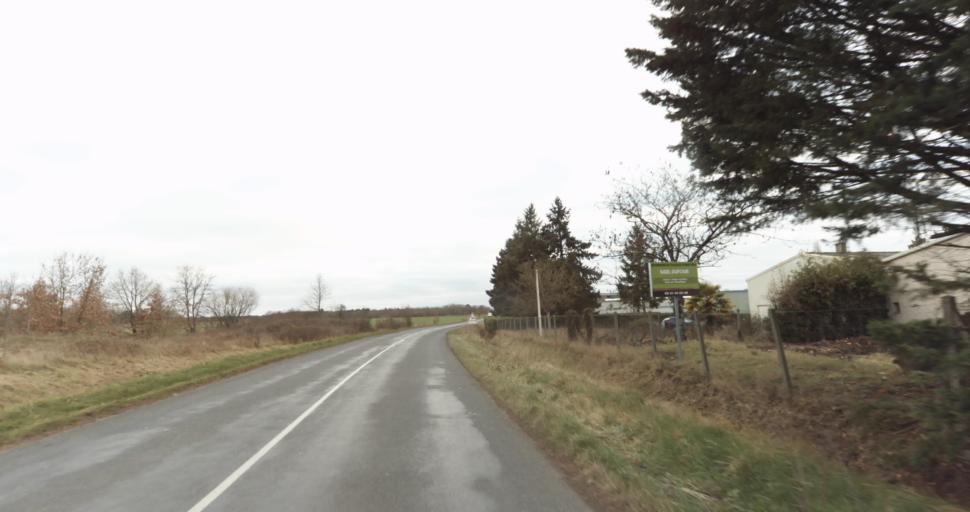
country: FR
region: Pays de la Loire
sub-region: Departement de Maine-et-Loire
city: Gennes
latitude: 47.3309
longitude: -0.2361
